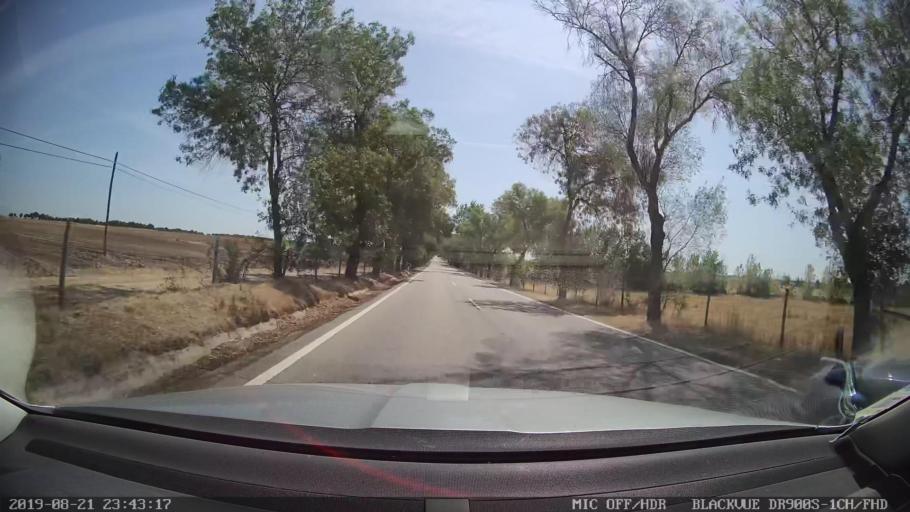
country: PT
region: Castelo Branco
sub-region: Idanha-A-Nova
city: Idanha-a-Nova
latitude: 39.8507
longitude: -7.2979
